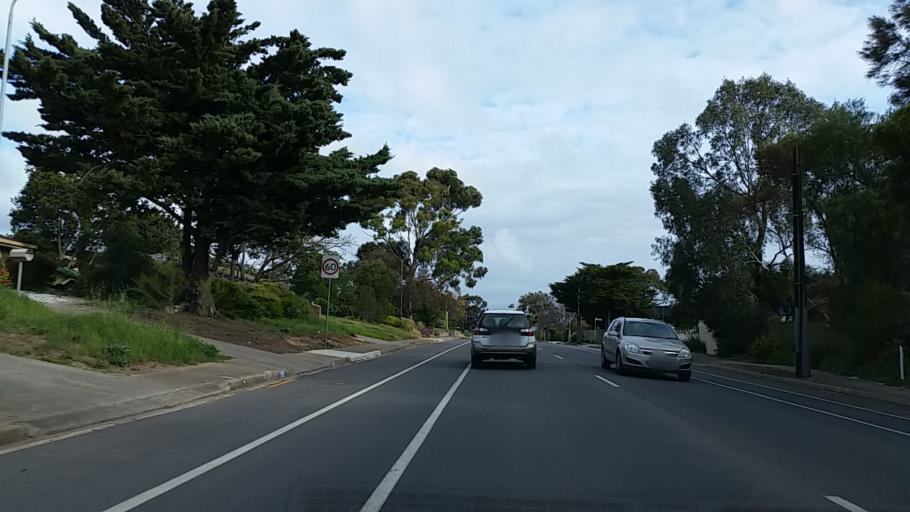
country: AU
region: South Australia
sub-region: Onkaparinga
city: Reynella
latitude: -35.1158
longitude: 138.5356
